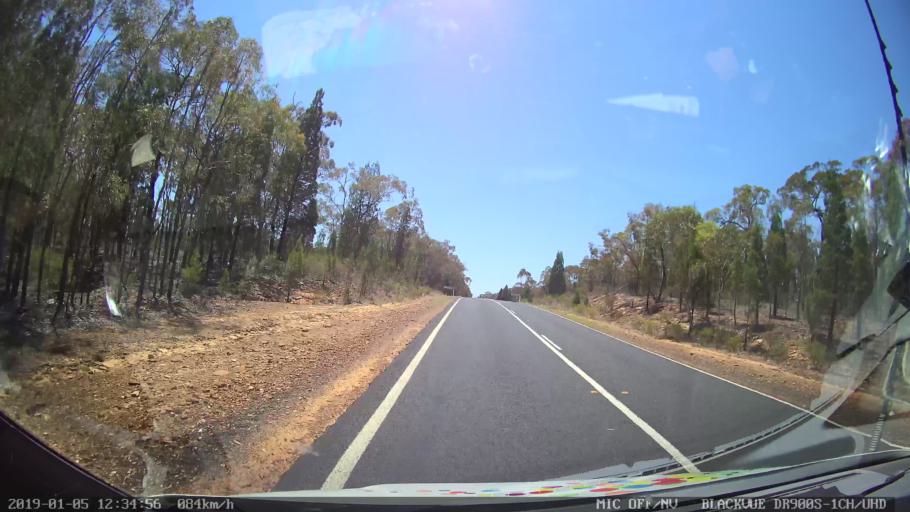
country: AU
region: New South Wales
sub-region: Warrumbungle Shire
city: Coonabarabran
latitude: -31.2107
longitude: 149.4179
